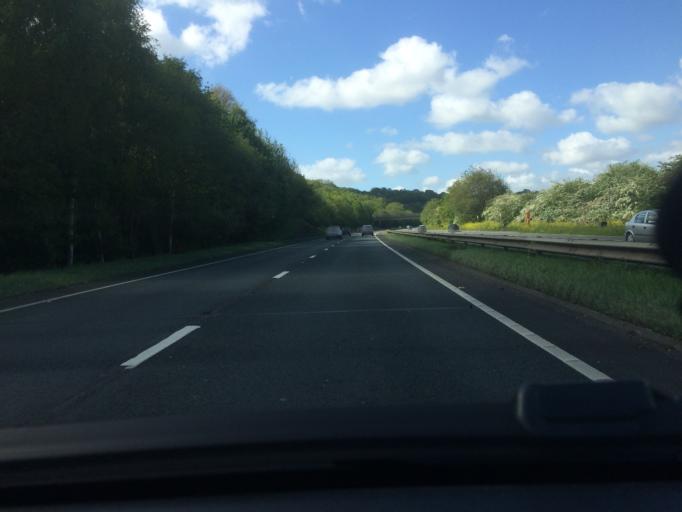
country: GB
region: Wales
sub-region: Wrexham
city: Gresford
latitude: 53.0969
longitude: -2.9659
